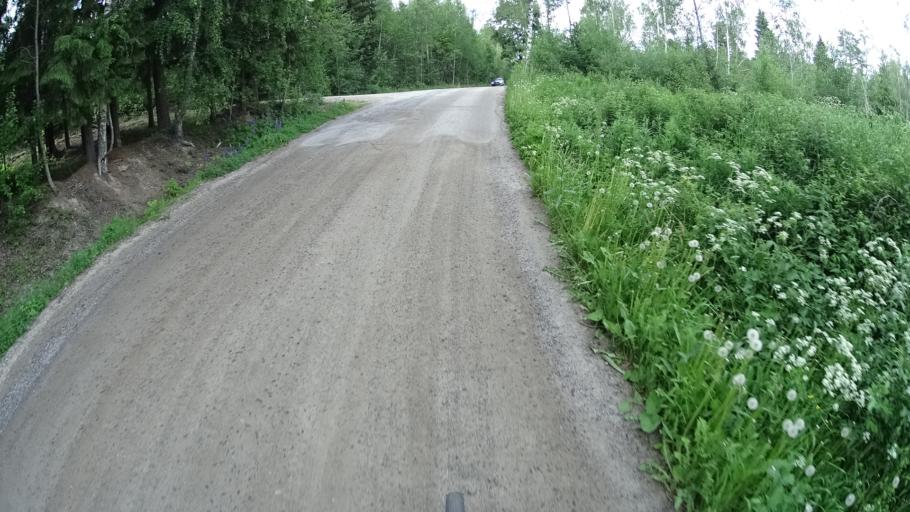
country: FI
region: Uusimaa
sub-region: Helsinki
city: Sibbo
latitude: 60.2877
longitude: 25.3107
